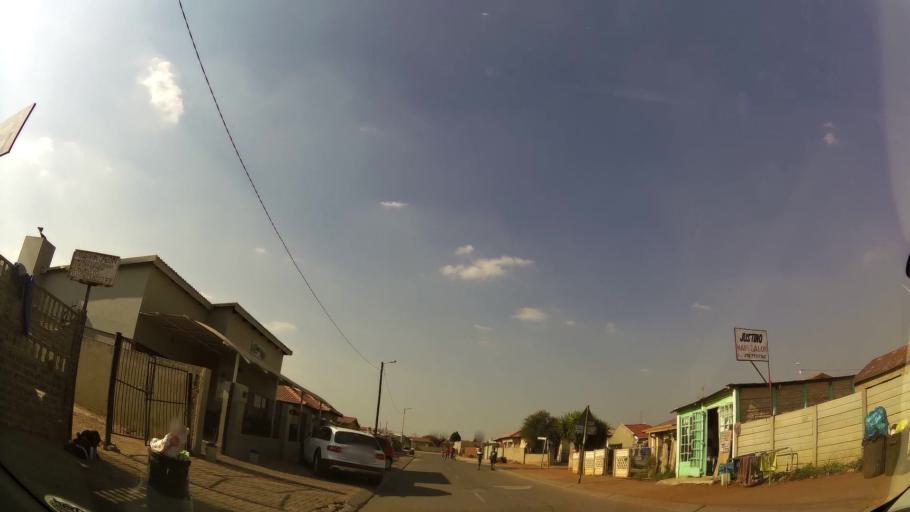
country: ZA
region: Gauteng
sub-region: Ekurhuleni Metropolitan Municipality
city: Brakpan
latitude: -26.1569
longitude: 28.4078
